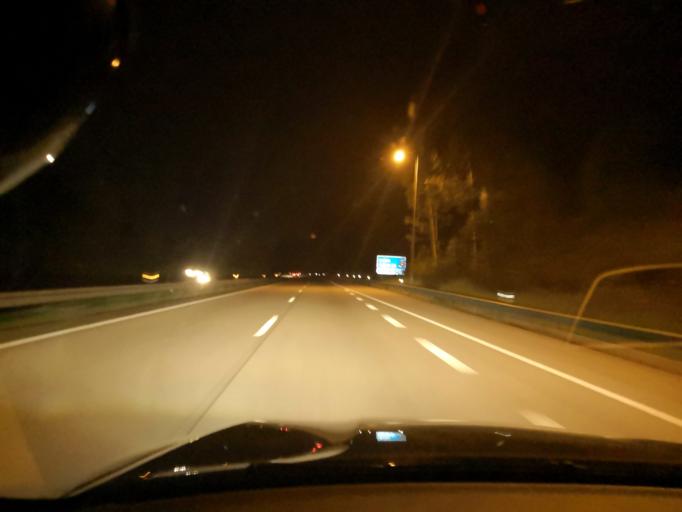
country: PT
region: Aveiro
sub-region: Albergaria-A-Velha
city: Albergaria-a-Velha
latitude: 40.6775
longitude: -8.4473
